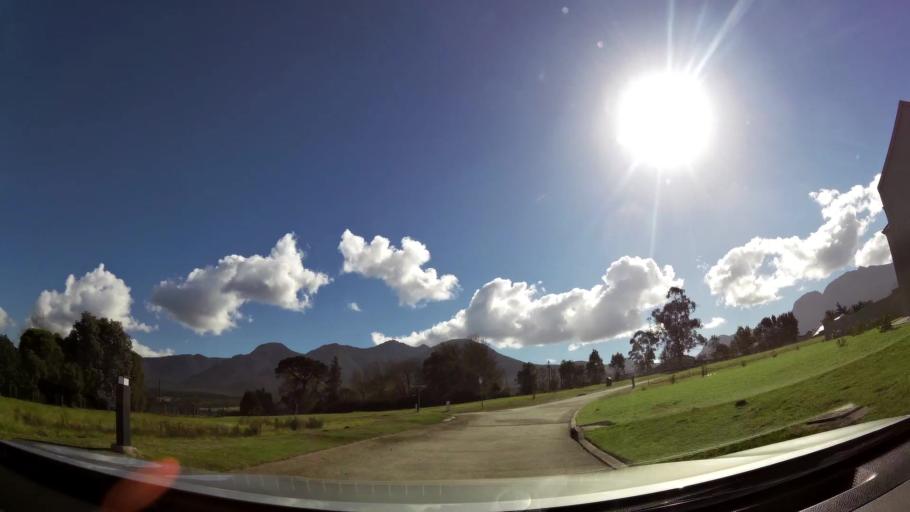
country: ZA
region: Western Cape
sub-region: Eden District Municipality
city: George
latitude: -33.9409
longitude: 22.4039
